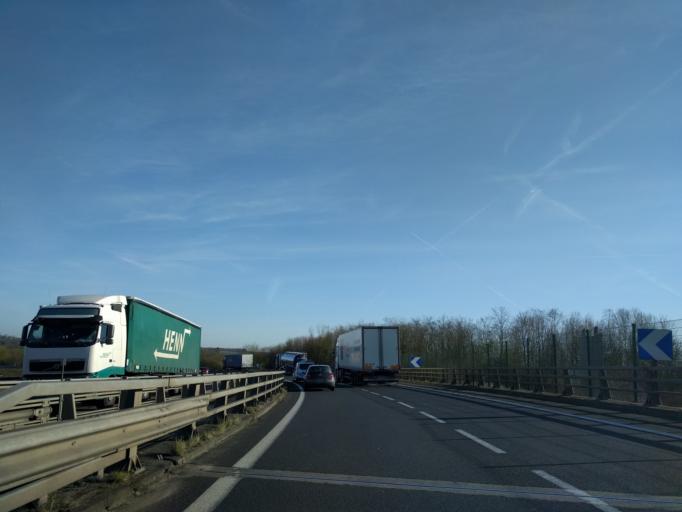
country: FR
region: Ile-de-France
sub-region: Departement de Seine-et-Marne
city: Brie-Comte-Robert
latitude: 48.6539
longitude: 2.6154
